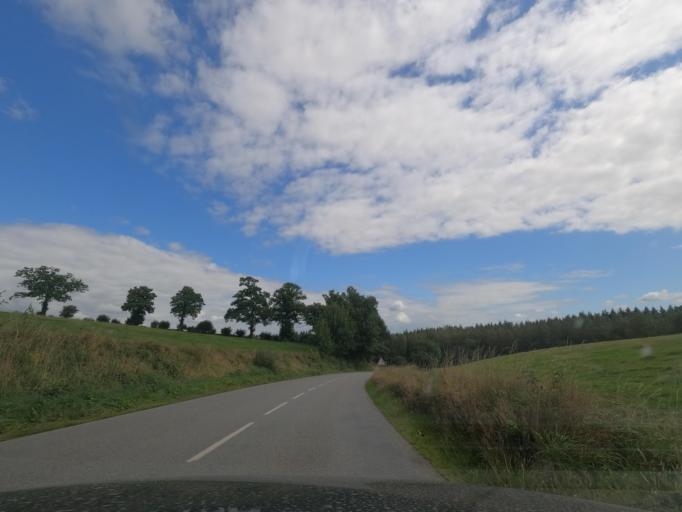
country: FR
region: Pays de la Loire
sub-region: Departement de la Mayenne
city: Landivy
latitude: 48.4779
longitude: -1.0058
